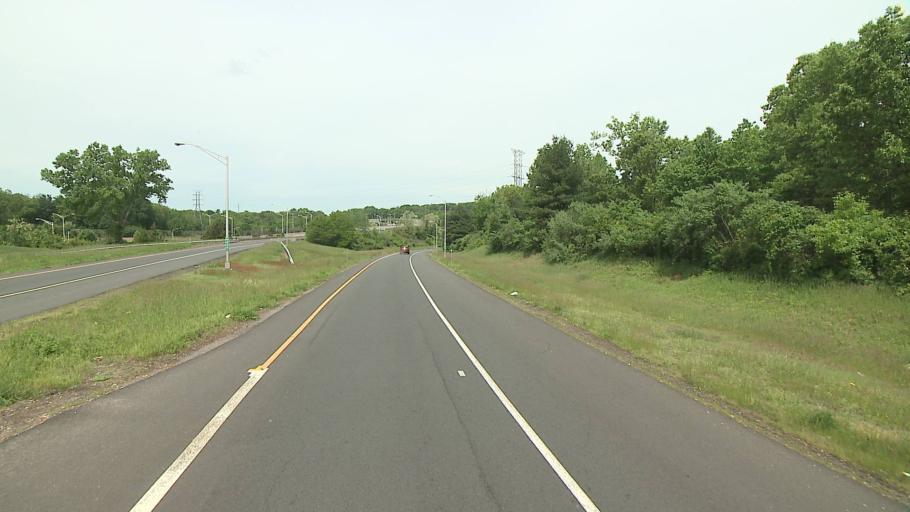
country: US
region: Connecticut
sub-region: Hartford County
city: East Hartford
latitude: 41.7681
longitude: -72.5749
